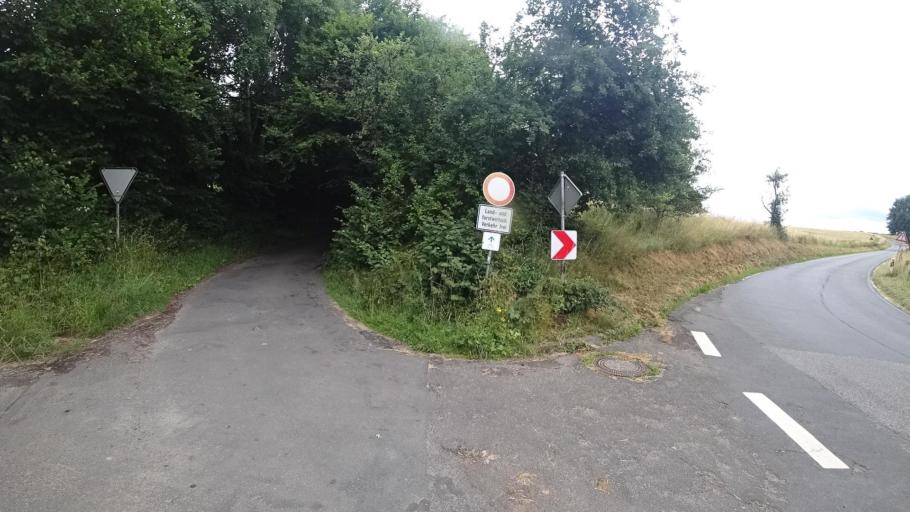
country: DE
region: Rheinland-Pfalz
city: Fiersbach
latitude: 50.6956
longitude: 7.4995
